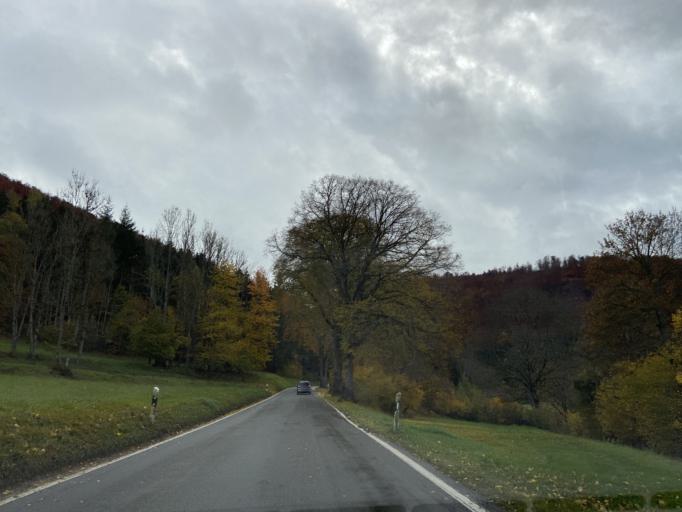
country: DE
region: Baden-Wuerttemberg
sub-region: Tuebingen Region
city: Schwenningen
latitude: 48.0778
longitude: 9.0347
